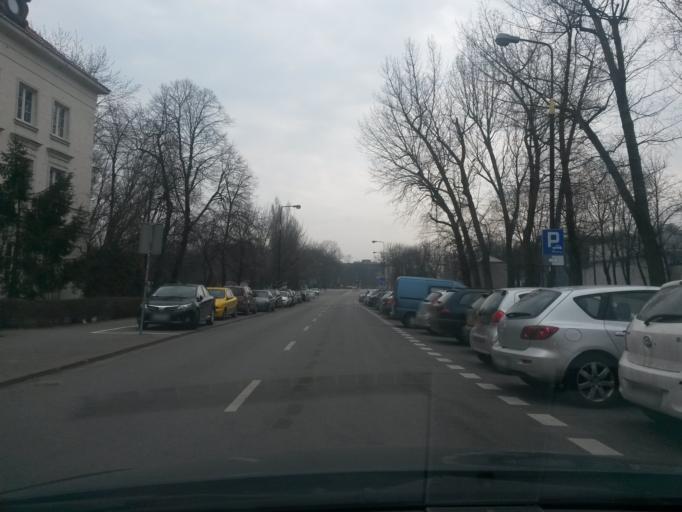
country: PL
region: Masovian Voivodeship
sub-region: Warszawa
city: Srodmiescie
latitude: 52.2448
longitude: 21.0185
